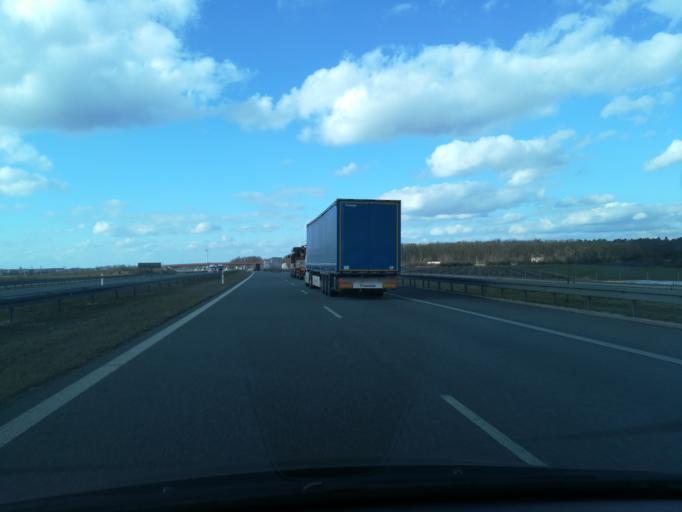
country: PL
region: Lodz Voivodeship
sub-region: Powiat kutnowski
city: Krzyzanow
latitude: 52.2500
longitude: 19.4466
